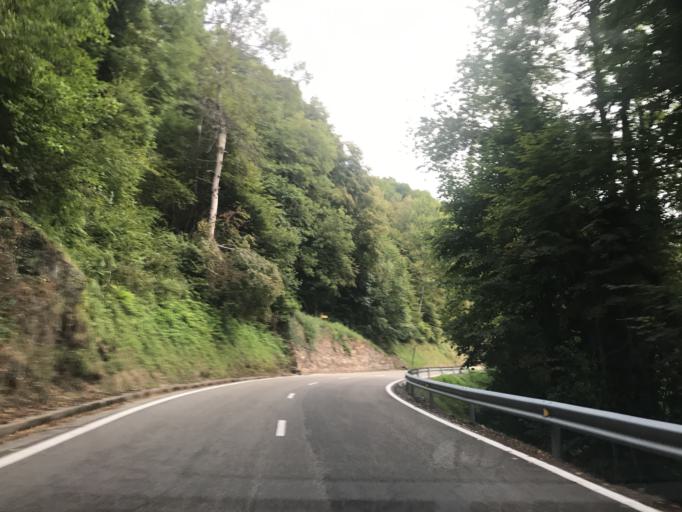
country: ES
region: Catalonia
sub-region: Provincia de Lleida
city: Les
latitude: 42.7753
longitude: 0.6804
